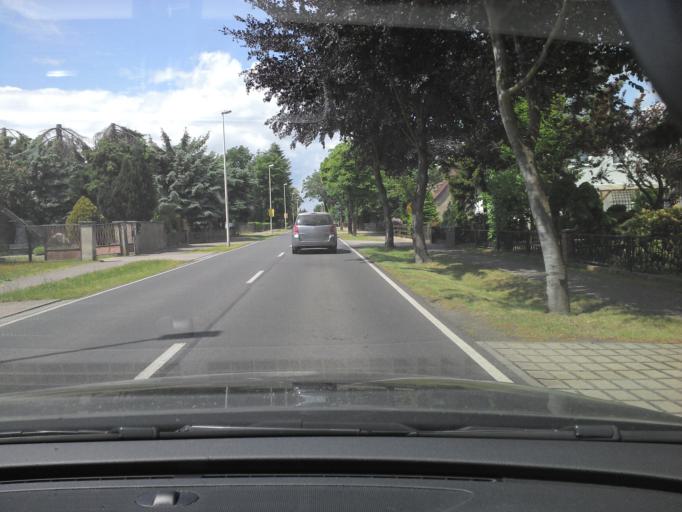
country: DE
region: Brandenburg
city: Werben
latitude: 51.8105
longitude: 14.1981
